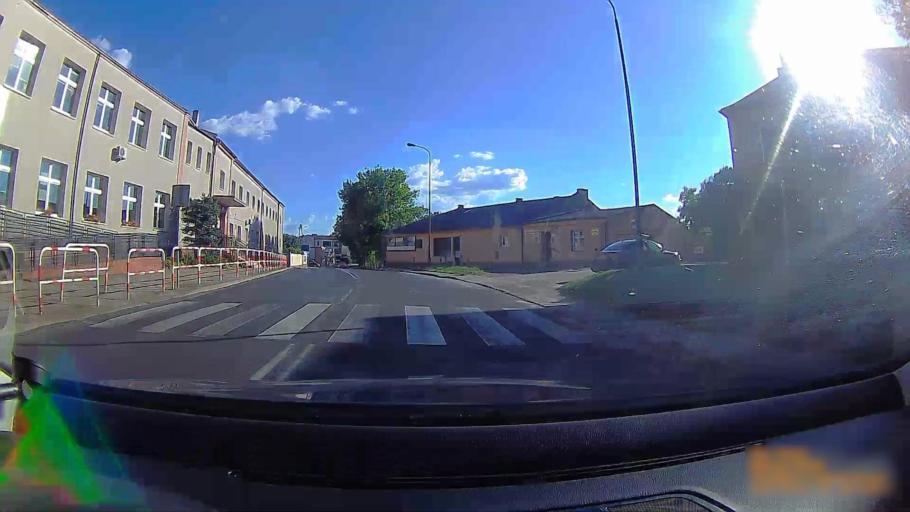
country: PL
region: Greater Poland Voivodeship
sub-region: Konin
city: Konin
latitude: 52.2031
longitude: 18.2488
